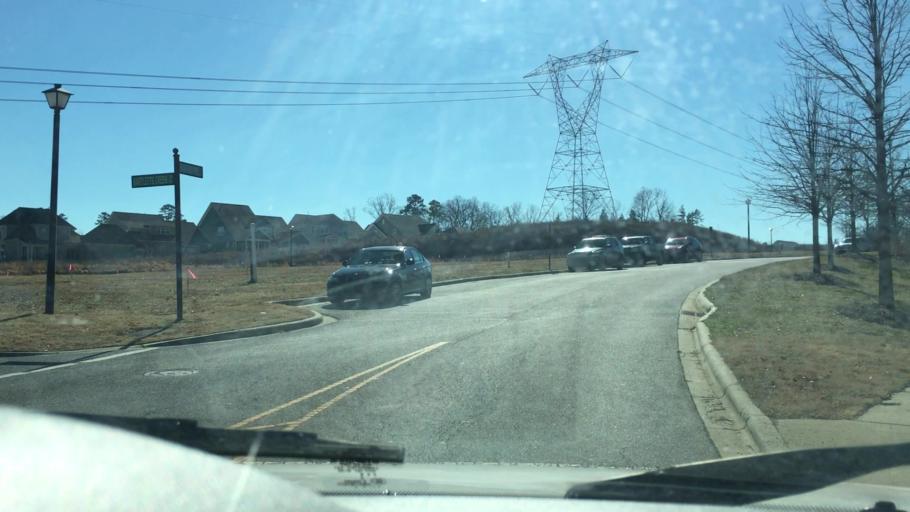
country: US
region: North Carolina
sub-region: Gaston County
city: Davidson
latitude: 35.4742
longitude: -80.8249
